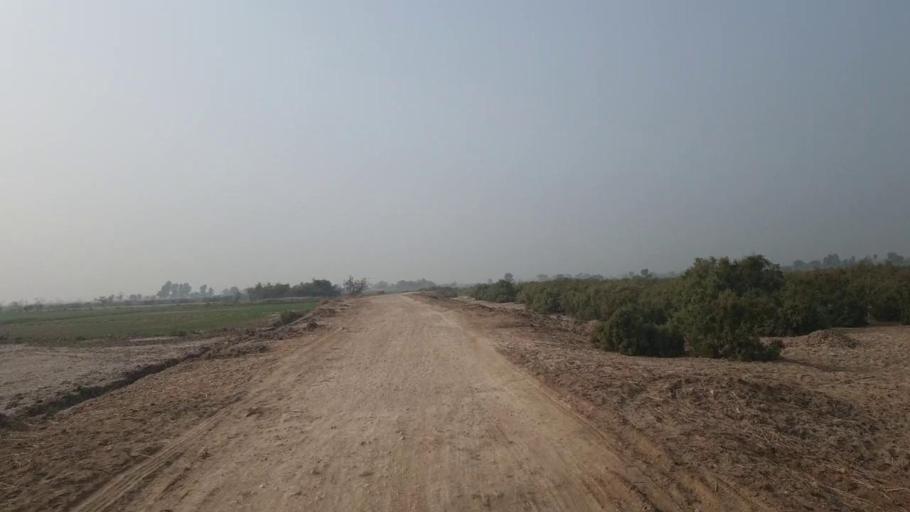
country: PK
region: Sindh
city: Bhit Shah
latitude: 25.8558
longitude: 68.5627
